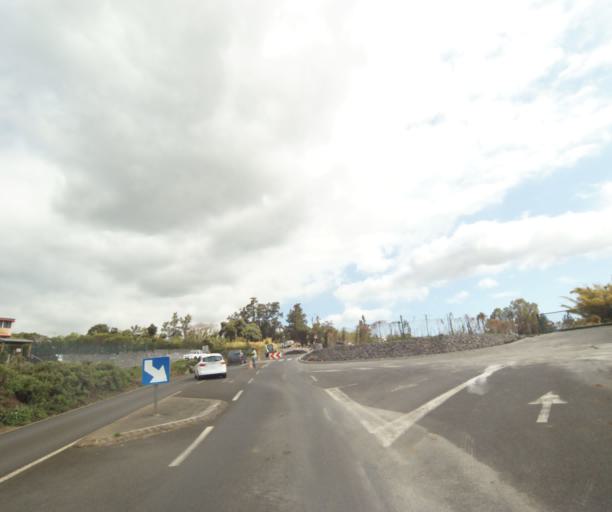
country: RE
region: Reunion
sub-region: Reunion
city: Saint-Paul
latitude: -21.0356
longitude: 55.2880
